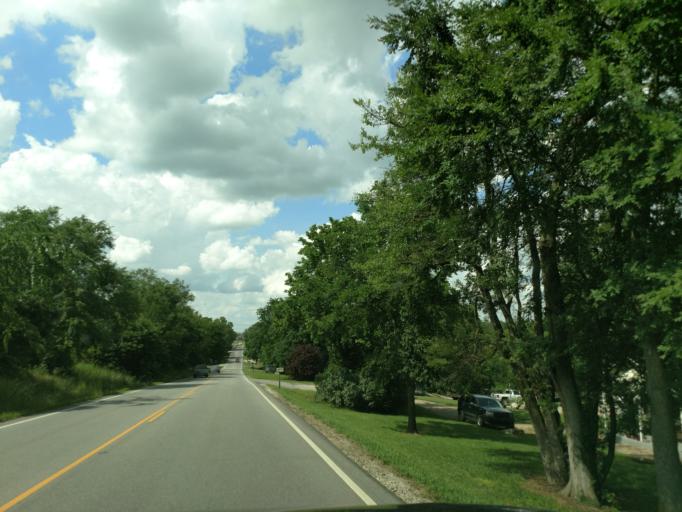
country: US
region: Arkansas
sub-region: Carroll County
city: Berryville
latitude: 36.3792
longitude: -93.5673
